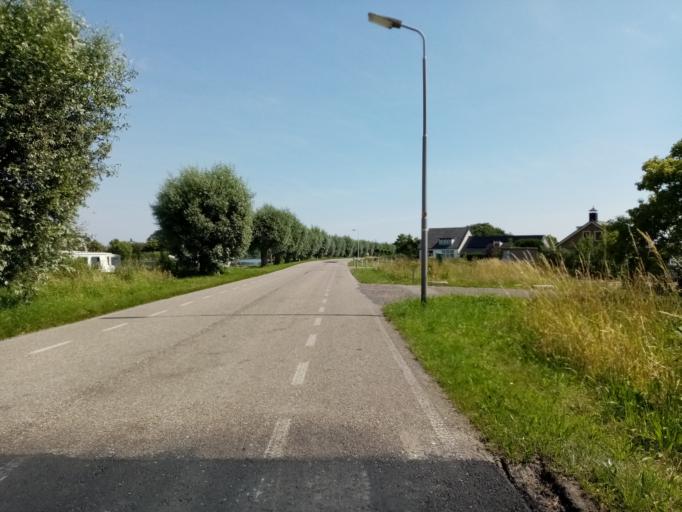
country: NL
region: North Holland
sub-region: Gemeente Aalsmeer
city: Aalsmeer
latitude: 52.2099
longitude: 4.7387
